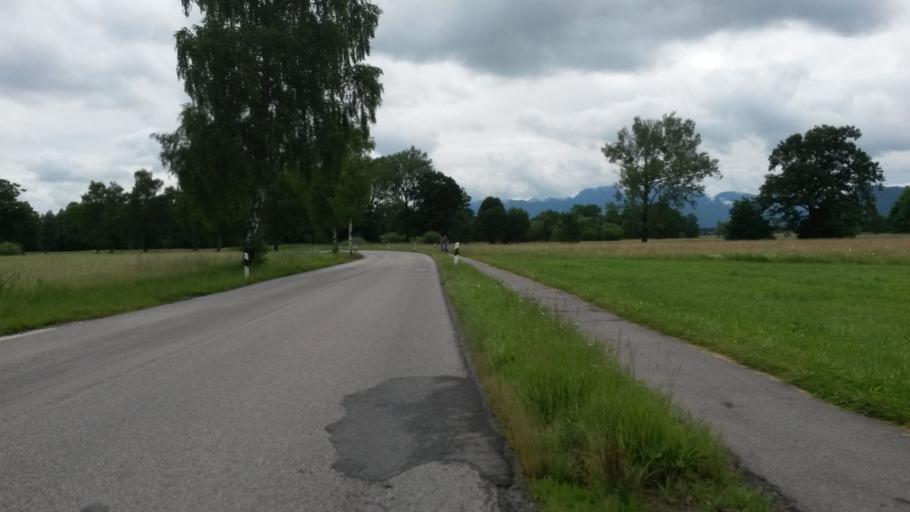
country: DE
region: Bavaria
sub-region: Upper Bavaria
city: Bernau am Chiemsee
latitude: 47.8369
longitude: 12.3660
